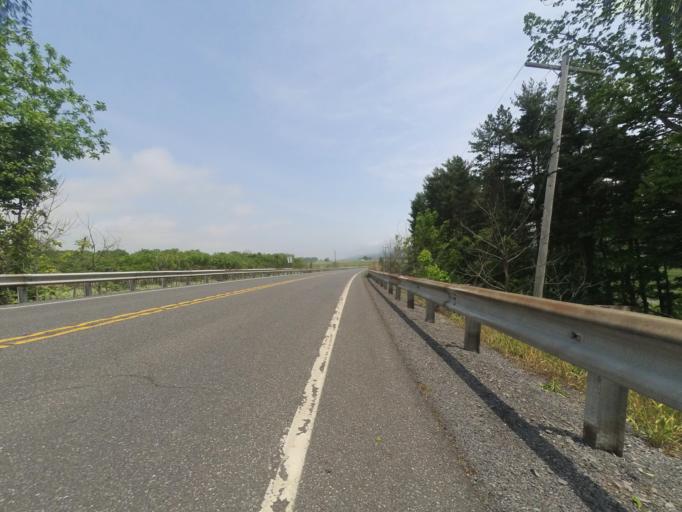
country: US
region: Pennsylvania
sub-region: Centre County
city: Pine Grove Mills
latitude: 40.7118
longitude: -77.9617
